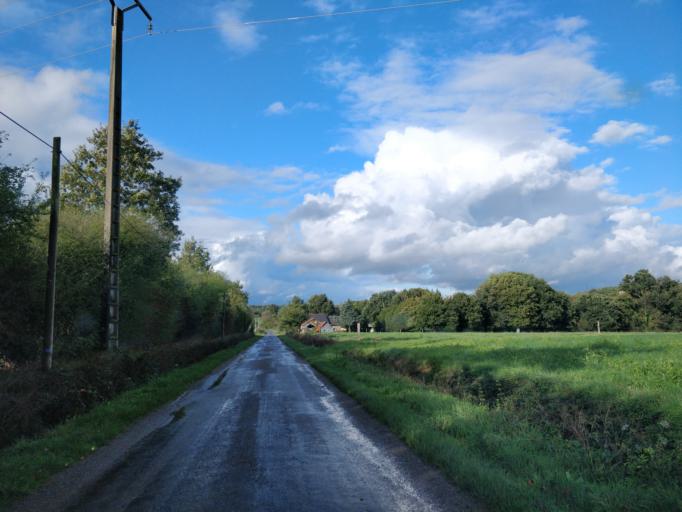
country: FR
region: Brittany
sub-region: Departement d'Ille-et-Vilaine
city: Chateaubourg
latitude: 48.1273
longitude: -1.4257
